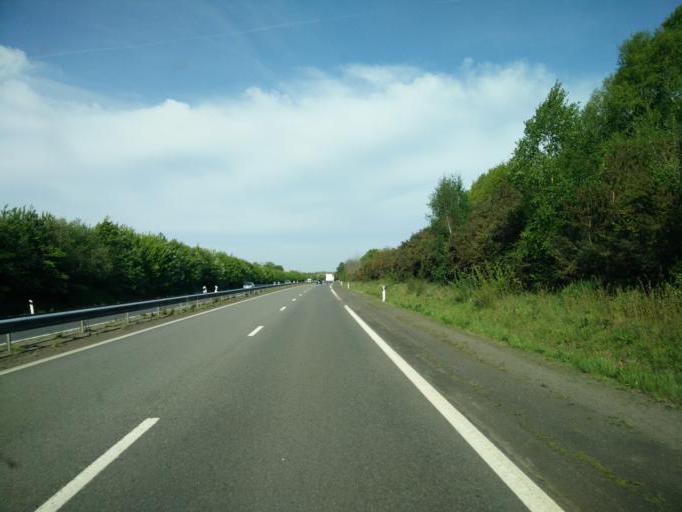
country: FR
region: Brittany
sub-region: Departement d'Ille-et-Vilaine
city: Saint-Broladre
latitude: 48.5631
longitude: -1.6290
